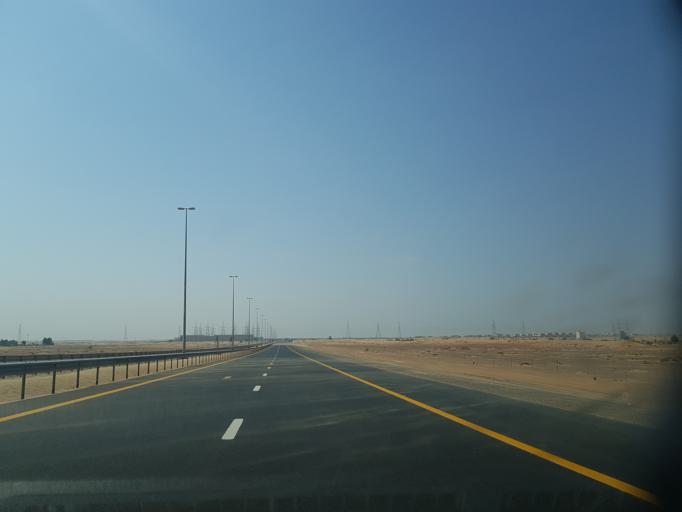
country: AE
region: Ash Shariqah
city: Sharjah
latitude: 25.2812
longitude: 55.6042
